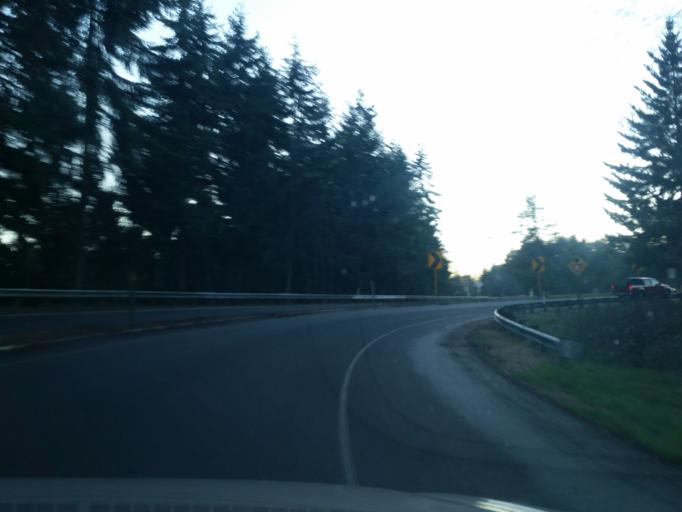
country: US
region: Washington
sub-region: Snohomish County
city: Mountlake Terrace
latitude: 47.7766
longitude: -122.3163
